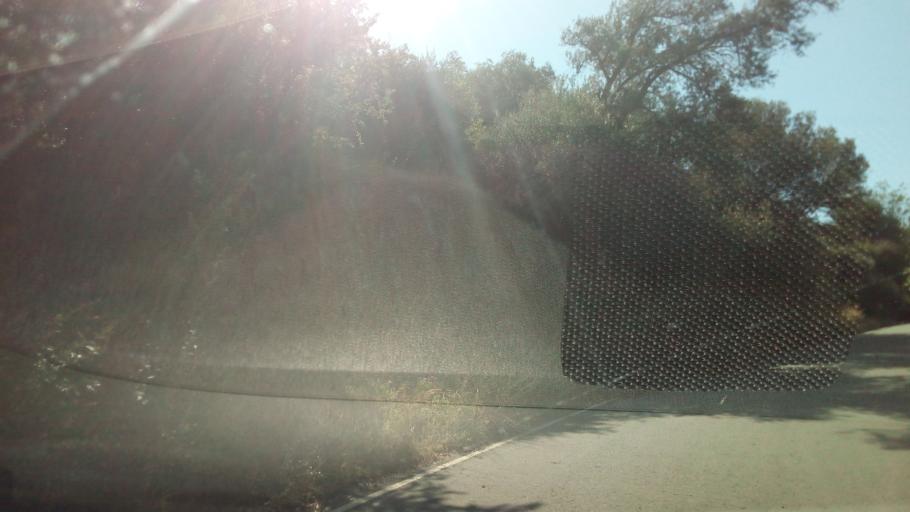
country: CY
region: Lefkosia
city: Lythrodontas
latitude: 34.8893
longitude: 33.2122
